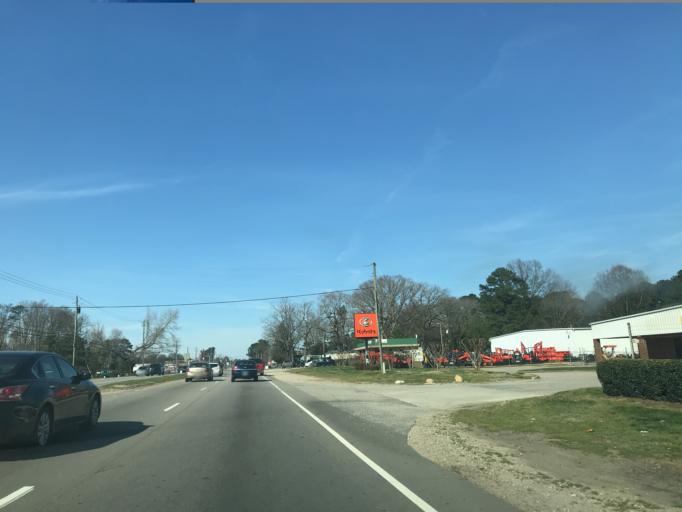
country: US
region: North Carolina
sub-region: Wake County
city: Garner
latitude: 35.7131
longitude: -78.6572
